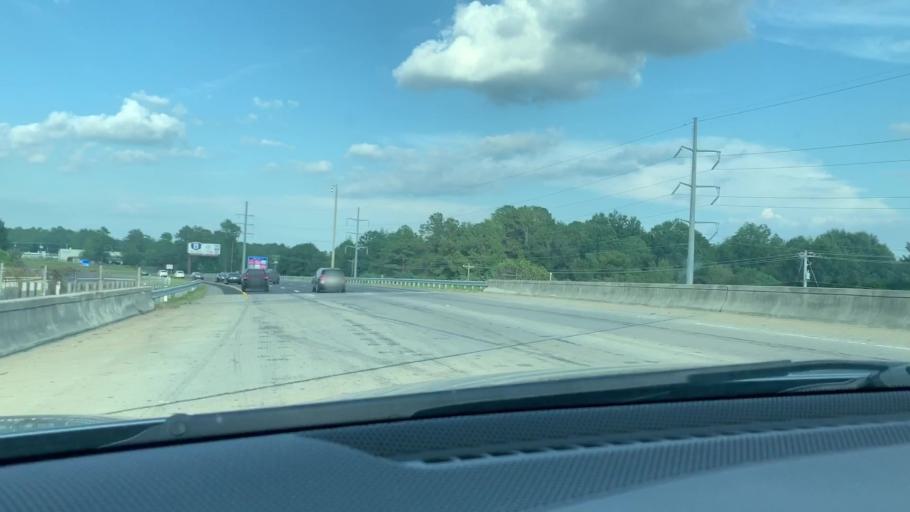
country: US
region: South Carolina
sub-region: Richland County
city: Forest Acres
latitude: 33.9551
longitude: -80.9579
